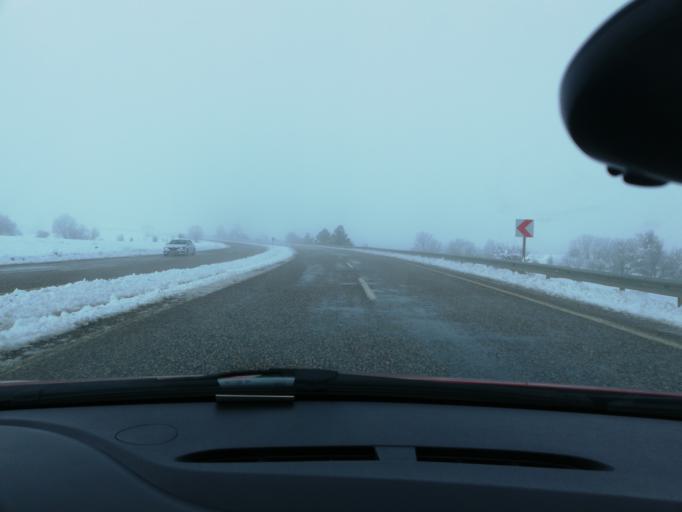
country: TR
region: Kastamonu
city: Akkaya
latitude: 41.2967
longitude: 33.4928
